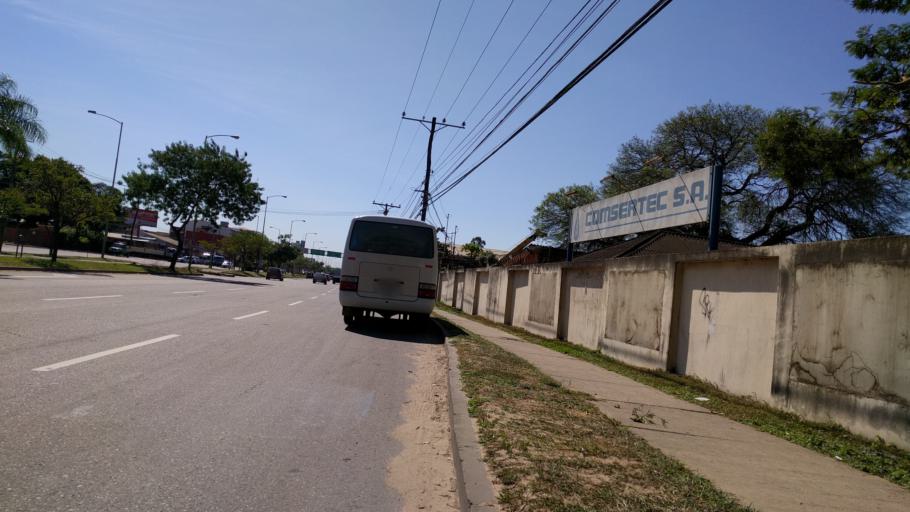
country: BO
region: Santa Cruz
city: Santa Cruz de la Sierra
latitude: -17.8146
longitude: -63.2111
